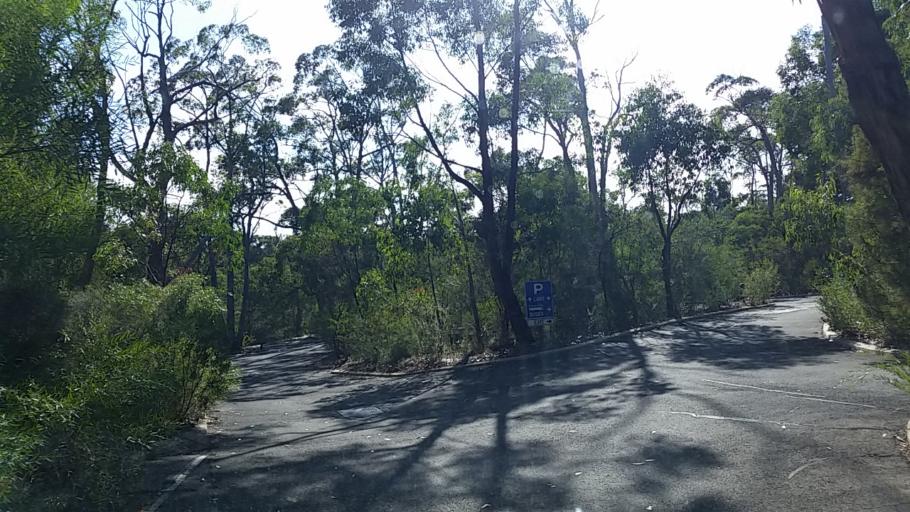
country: AU
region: South Australia
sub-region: Adelaide Hills
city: Crafers
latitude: -34.9664
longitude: 138.6971
